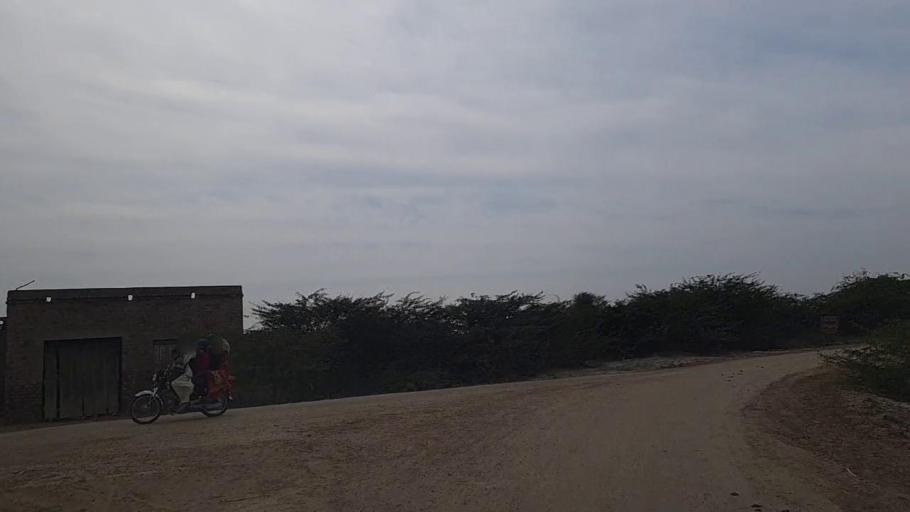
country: PK
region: Sindh
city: Daur
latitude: 26.4455
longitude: 68.4568
